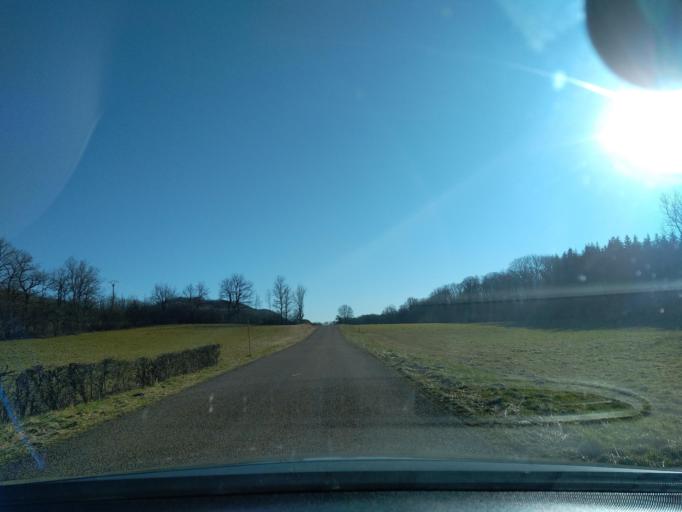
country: FR
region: Franche-Comte
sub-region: Departement du Jura
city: Poligny
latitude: 46.7134
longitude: 5.7378
